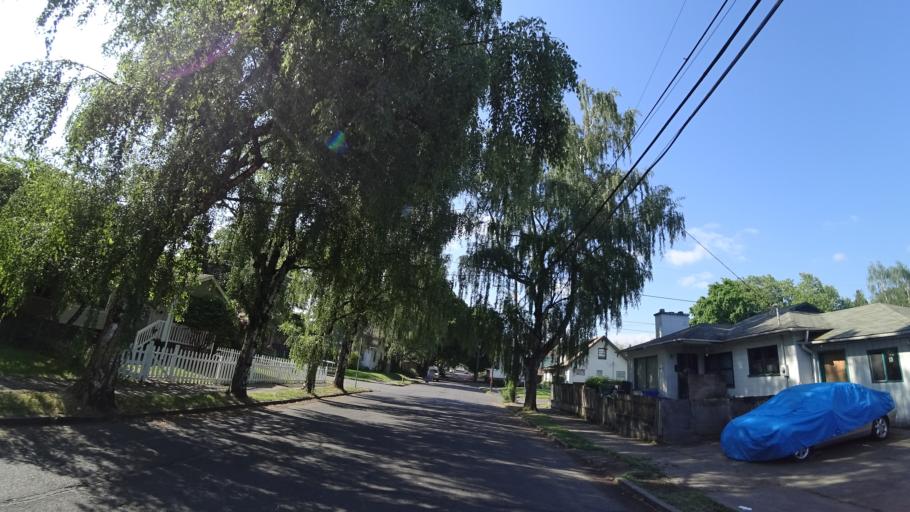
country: US
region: Oregon
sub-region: Multnomah County
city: Portland
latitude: 45.5745
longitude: -122.6501
